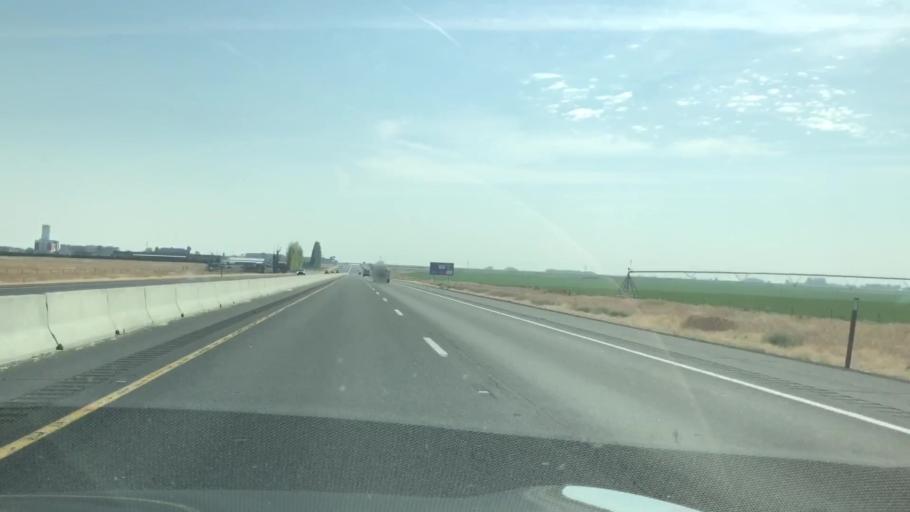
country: US
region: Washington
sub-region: Grant County
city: Moses Lake
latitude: 47.1014
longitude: -119.2677
